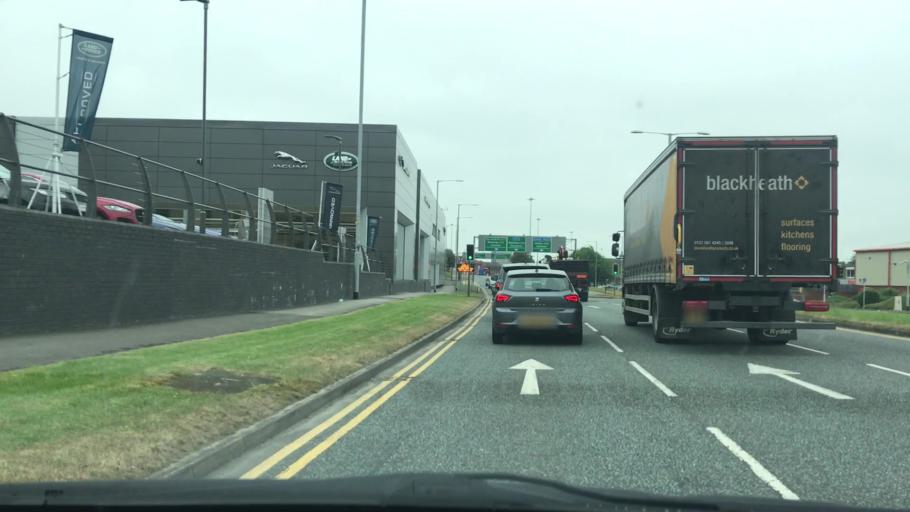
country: GB
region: England
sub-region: City and Borough of Leeds
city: Chapel Allerton
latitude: 53.8121
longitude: -1.5377
